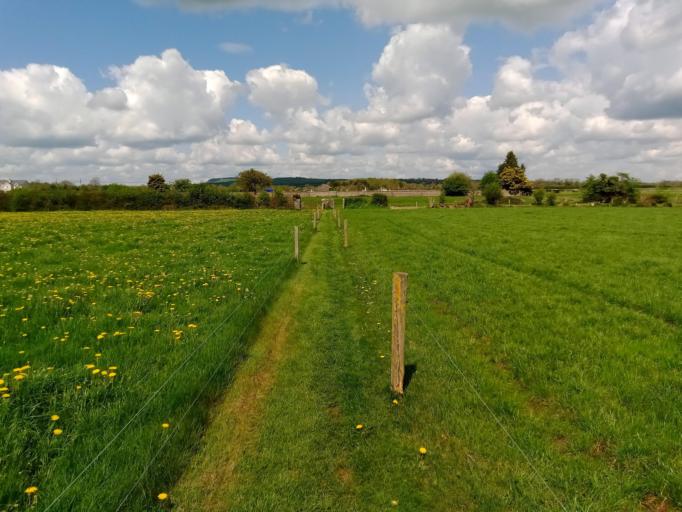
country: IE
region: Leinster
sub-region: Kilkenny
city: Ballyragget
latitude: 52.7343
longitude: -7.4166
